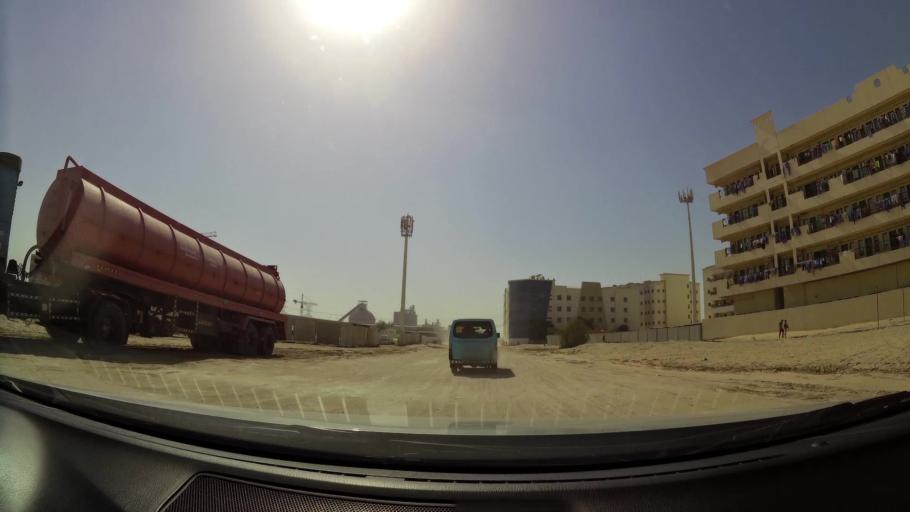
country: AE
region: Dubai
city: Dubai
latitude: 24.9966
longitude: 55.1426
